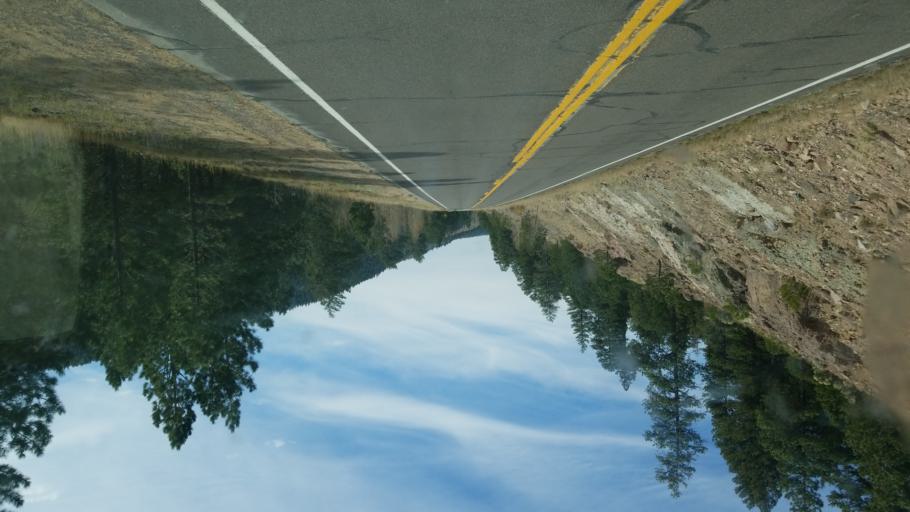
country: US
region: Colorado
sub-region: Conejos County
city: Conejos
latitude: 37.0755
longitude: -106.2835
